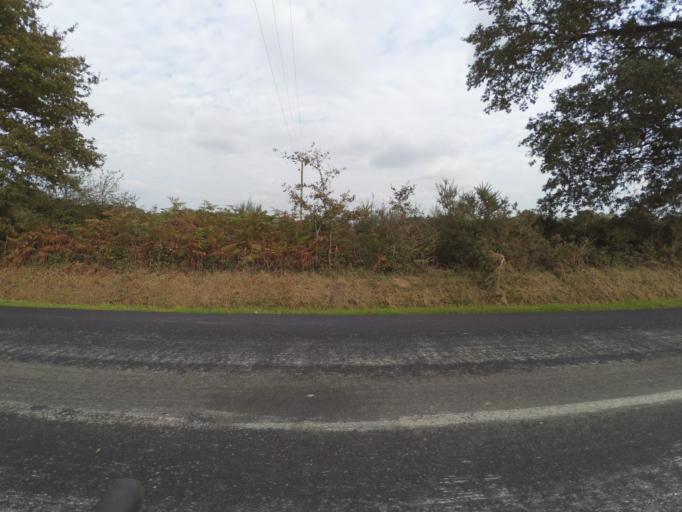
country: FR
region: Pays de la Loire
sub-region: Departement de la Vendee
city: Saint-Hilaire-de-Loulay
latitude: 46.9926
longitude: -1.3678
